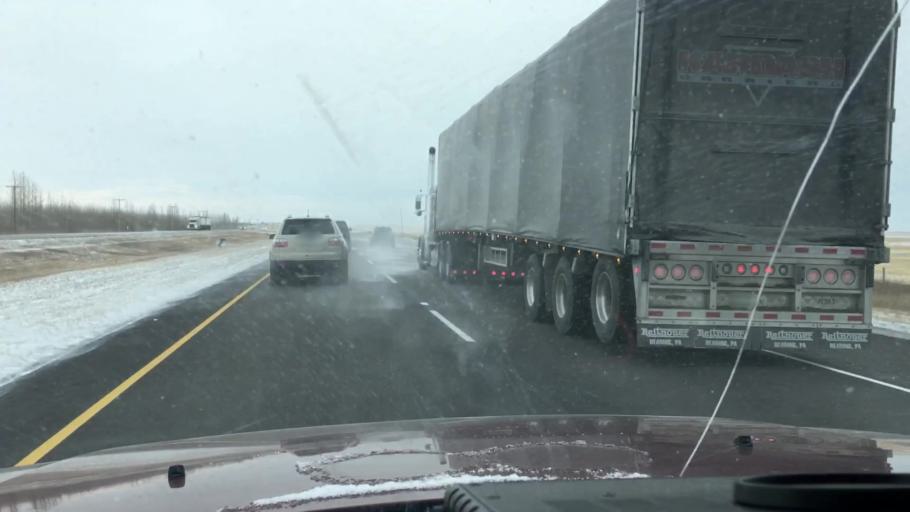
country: CA
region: Saskatchewan
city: Saskatoon
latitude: 51.7722
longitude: -106.4763
